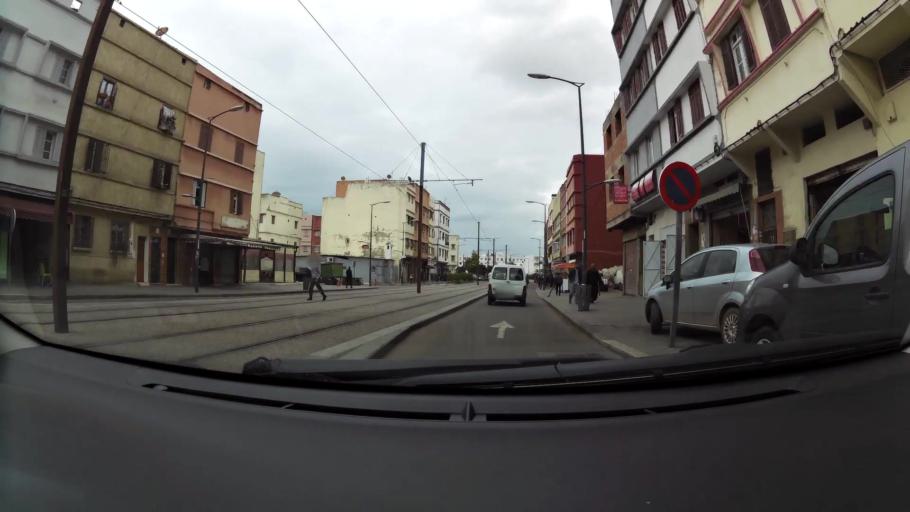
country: MA
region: Grand Casablanca
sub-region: Casablanca
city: Casablanca
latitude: 33.5826
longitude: -7.5670
